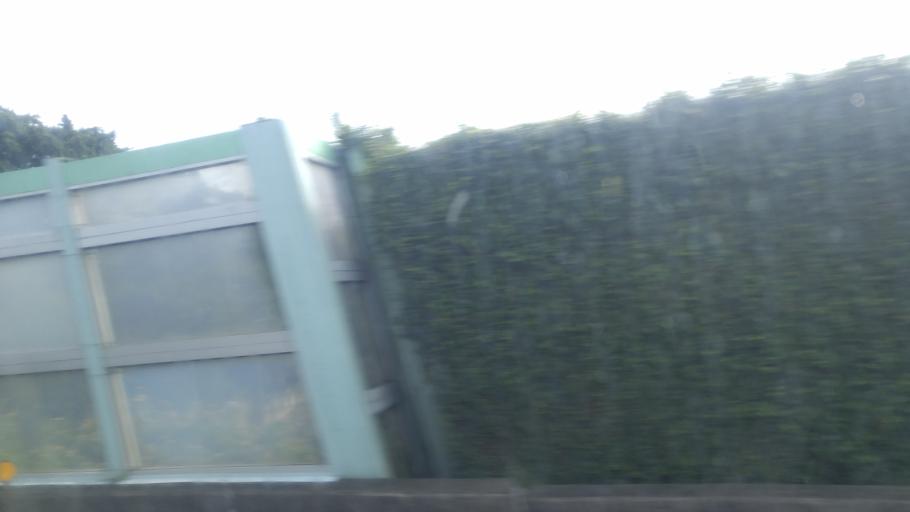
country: TW
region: Taiwan
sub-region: Hsinchu
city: Zhubei
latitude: 24.8934
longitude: 121.1253
